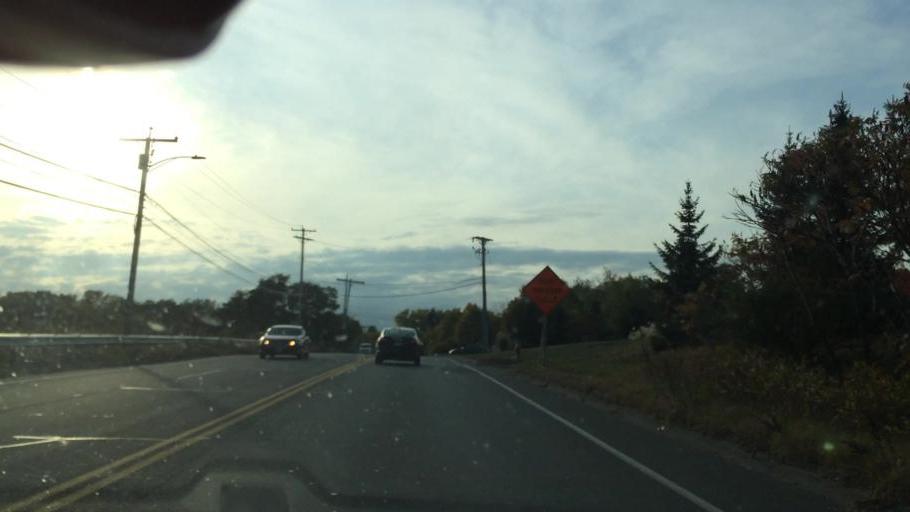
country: US
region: Massachusetts
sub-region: Essex County
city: Lawrence
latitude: 42.7447
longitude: -71.1431
